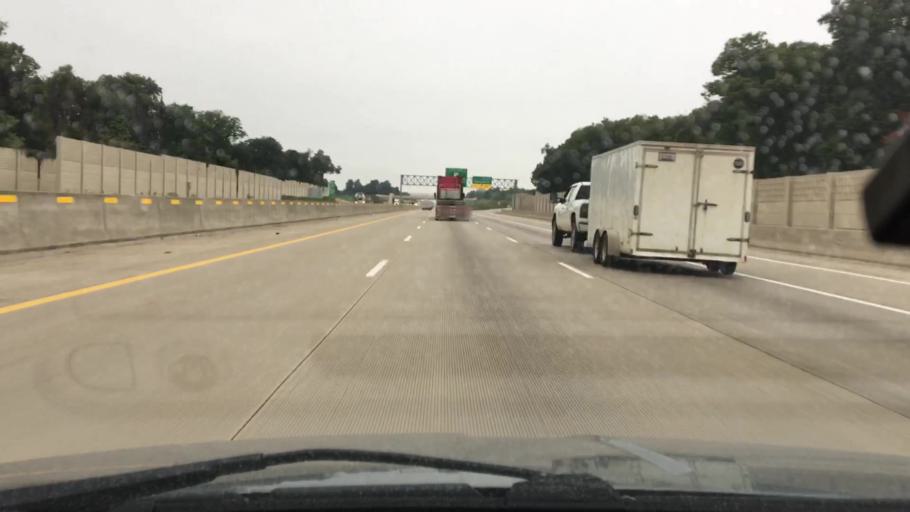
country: US
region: Michigan
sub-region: Kalamazoo County
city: Portage
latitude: 42.2369
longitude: -85.5959
